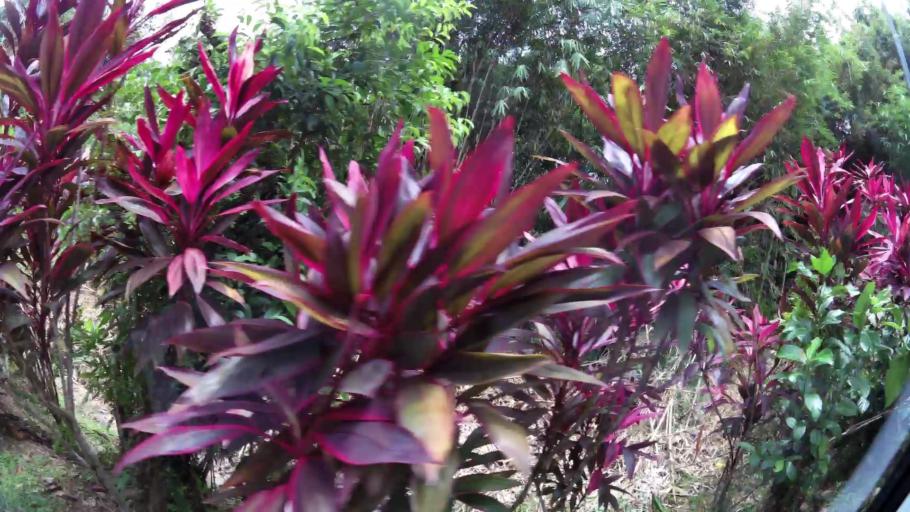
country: BN
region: Brunei and Muara
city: Bandar Seri Begawan
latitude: 4.9000
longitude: 114.9158
